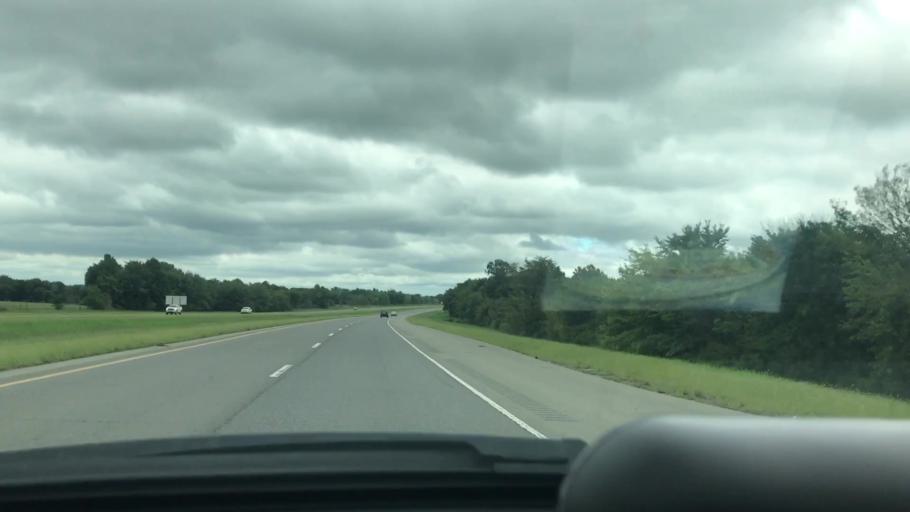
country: US
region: Oklahoma
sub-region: McIntosh County
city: Checotah
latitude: 35.5811
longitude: -95.4906
